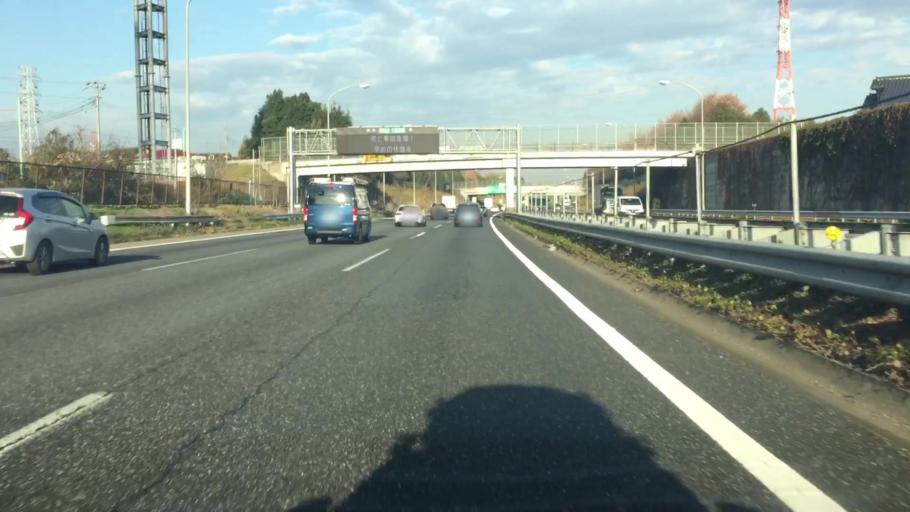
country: JP
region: Saitama
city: Sakado
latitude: 35.9202
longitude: 139.4162
